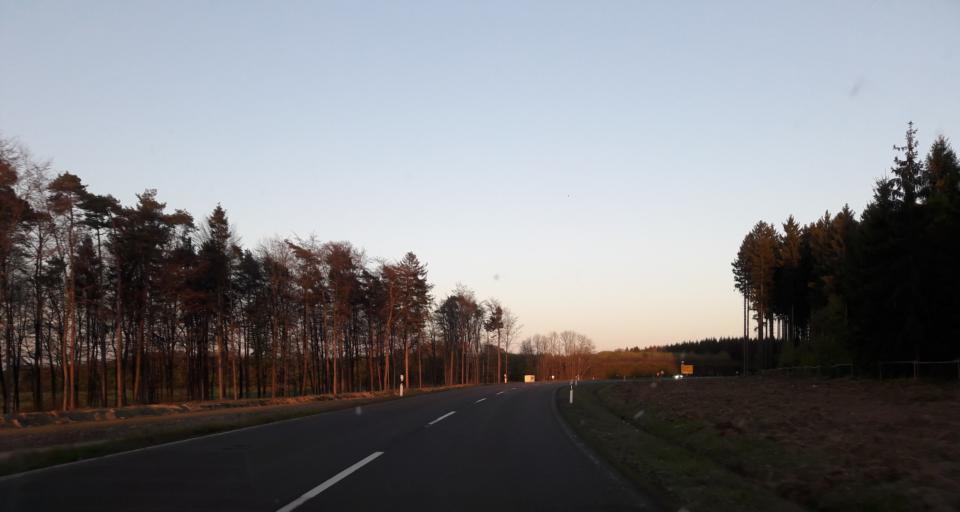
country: DE
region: Rheinland-Pfalz
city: Kommen
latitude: 49.8709
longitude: 7.1306
